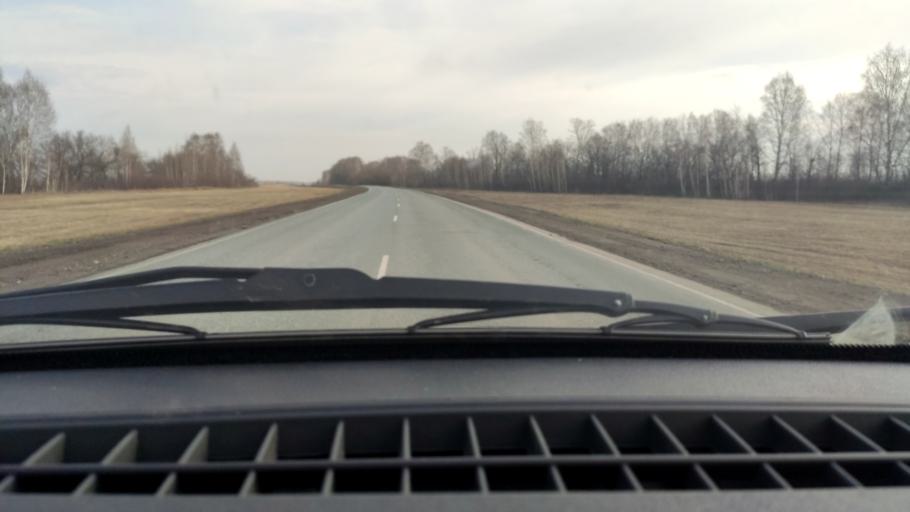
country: RU
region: Bashkortostan
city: Chishmy
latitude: 54.4080
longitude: 55.2191
